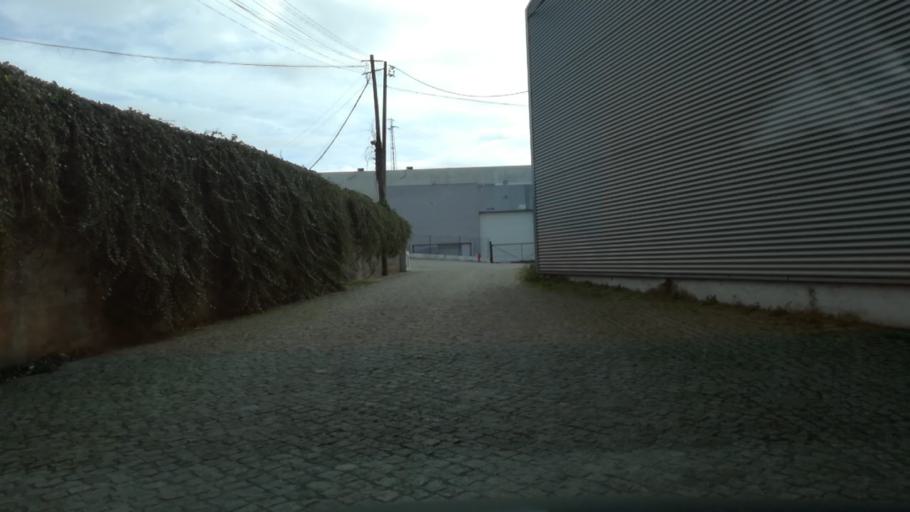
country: PT
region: Porto
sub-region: Maia
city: Gemunde
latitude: 41.2542
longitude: -8.6694
